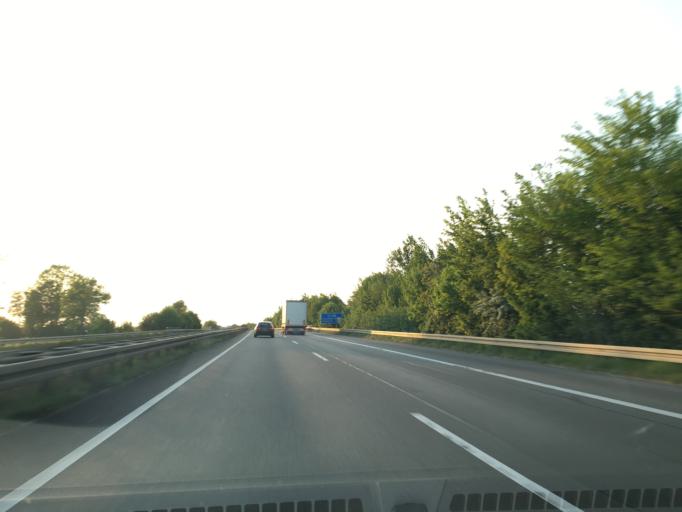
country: DE
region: Lower Saxony
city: Melle
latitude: 52.2016
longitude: 8.3086
